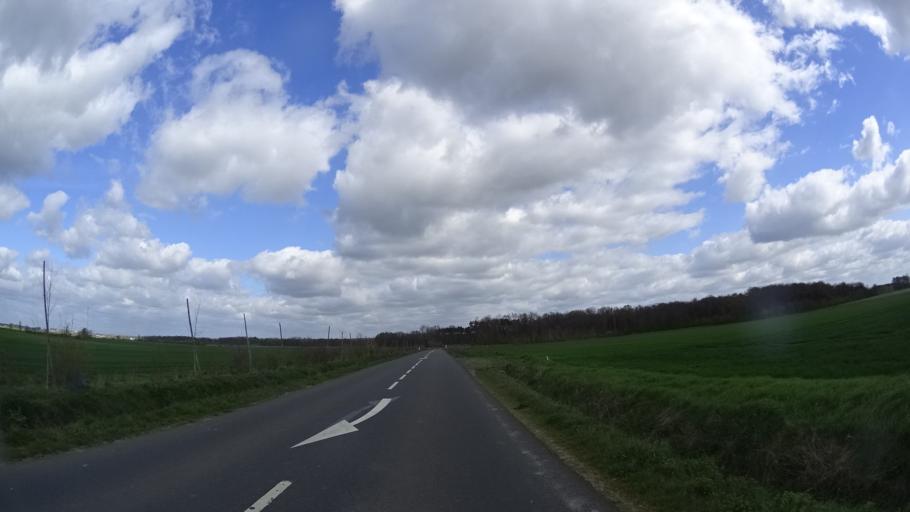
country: FR
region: Pays de la Loire
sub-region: Departement de Maine-et-Loire
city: Breze
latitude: 47.0830
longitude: -0.0130
